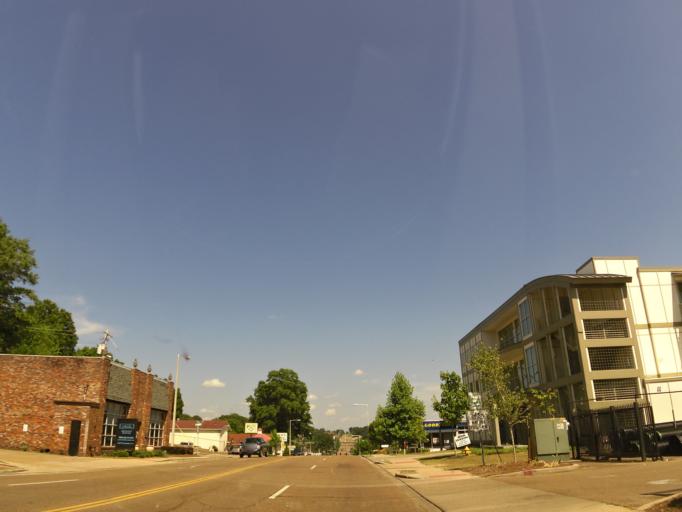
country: US
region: Mississippi
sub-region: Lafayette County
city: Oxford
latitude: 34.3637
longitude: -89.5171
